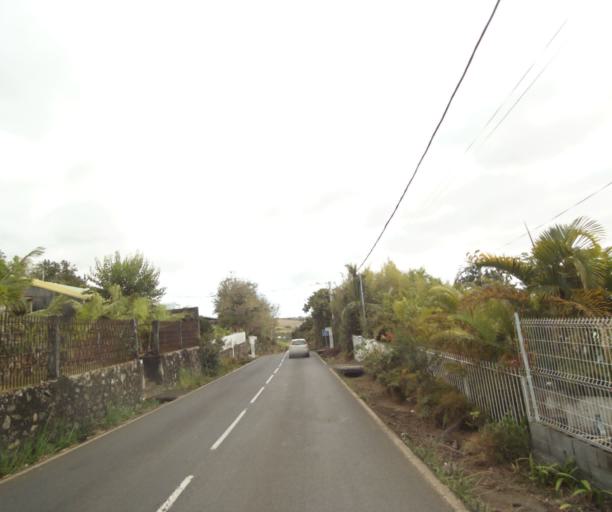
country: RE
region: Reunion
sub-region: Reunion
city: Saint-Paul
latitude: -21.0385
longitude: 55.2937
